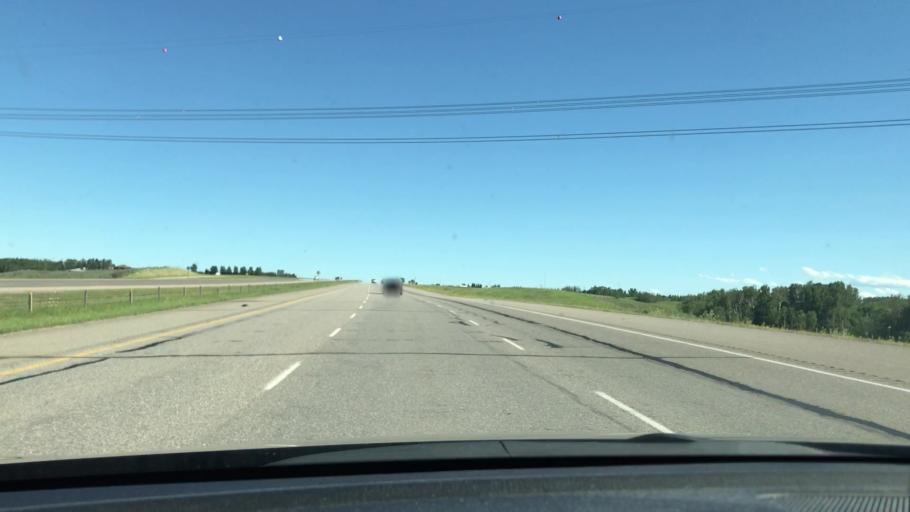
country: CA
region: Alberta
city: Crossfield
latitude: 51.4612
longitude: -114.0238
